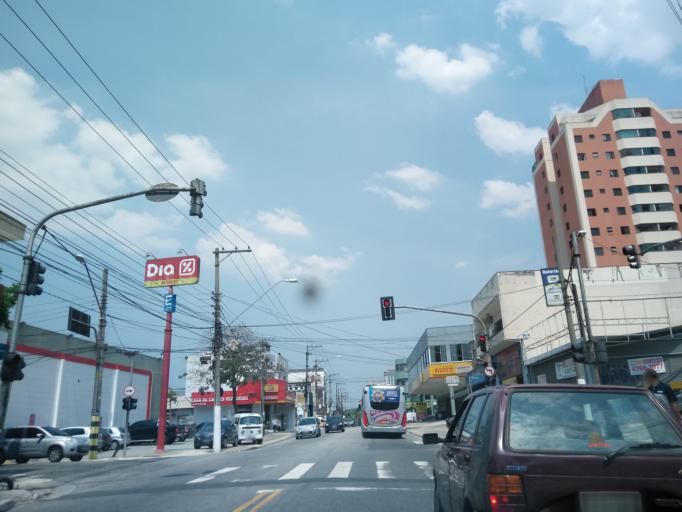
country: BR
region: Sao Paulo
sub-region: Santo Andre
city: Santo Andre
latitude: -23.6618
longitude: -46.5648
